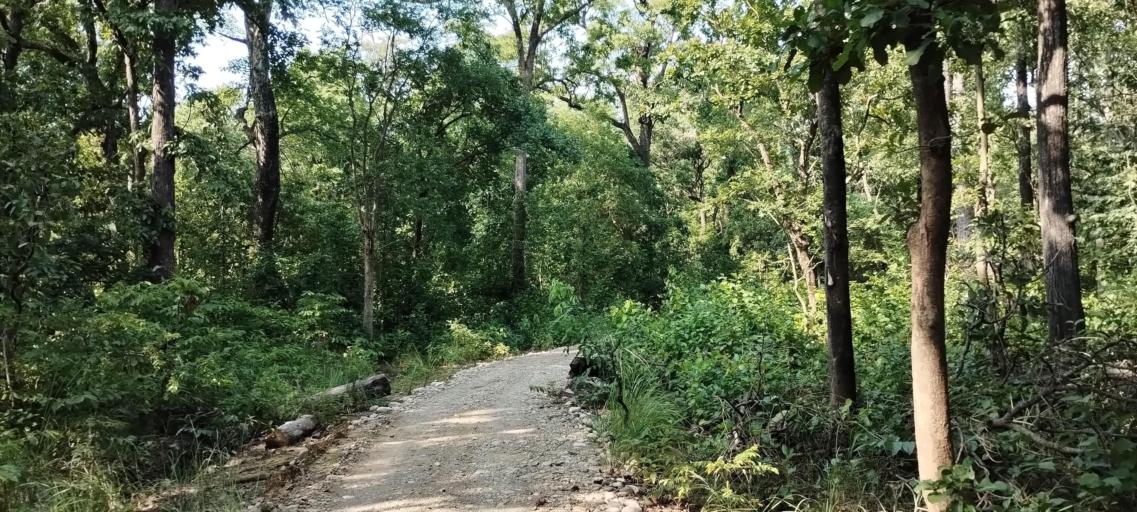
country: NP
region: Far Western
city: Tikapur
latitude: 28.5625
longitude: 81.2660
